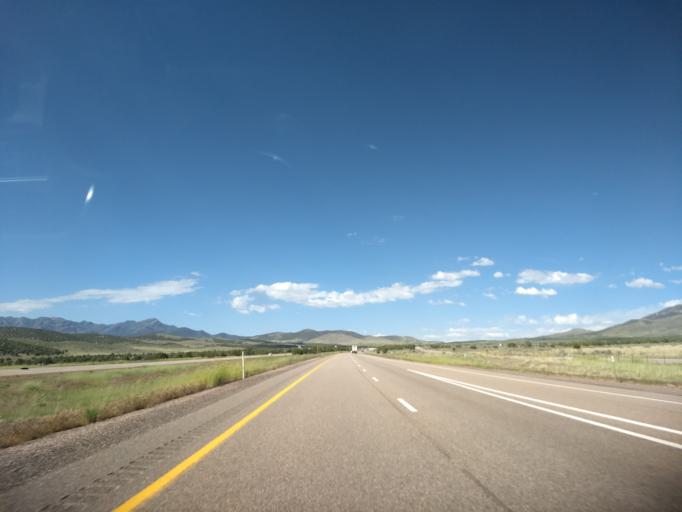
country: US
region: Utah
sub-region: Millard County
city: Fillmore
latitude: 39.1495
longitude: -112.2325
